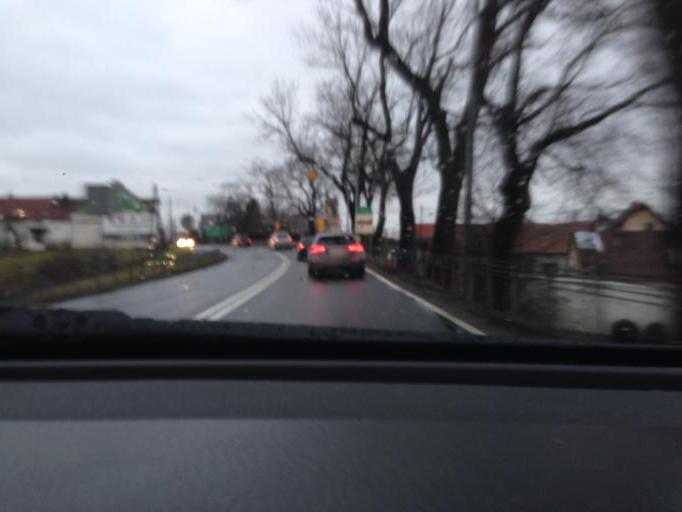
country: PL
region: Opole Voivodeship
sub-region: Powiat opolski
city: Opole
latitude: 50.6990
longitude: 17.9607
